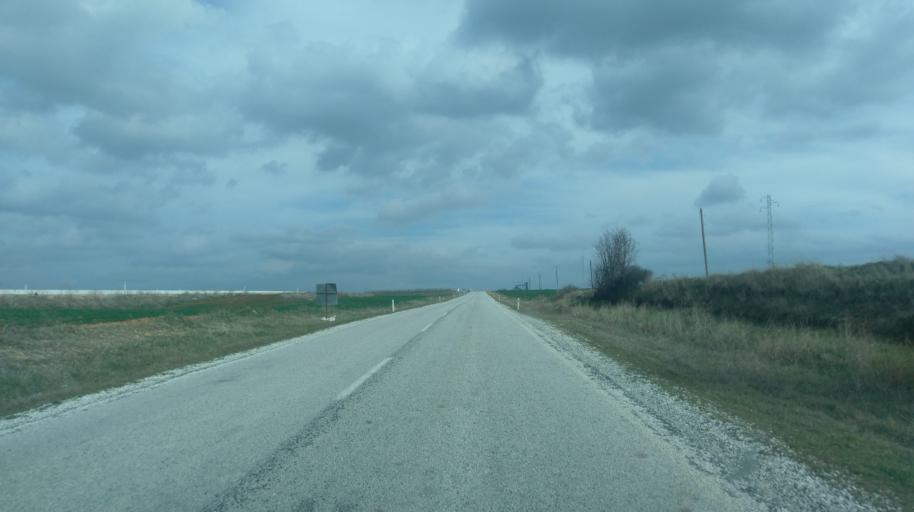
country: TR
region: Kirklareli
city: Inece
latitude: 41.6795
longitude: 27.0474
